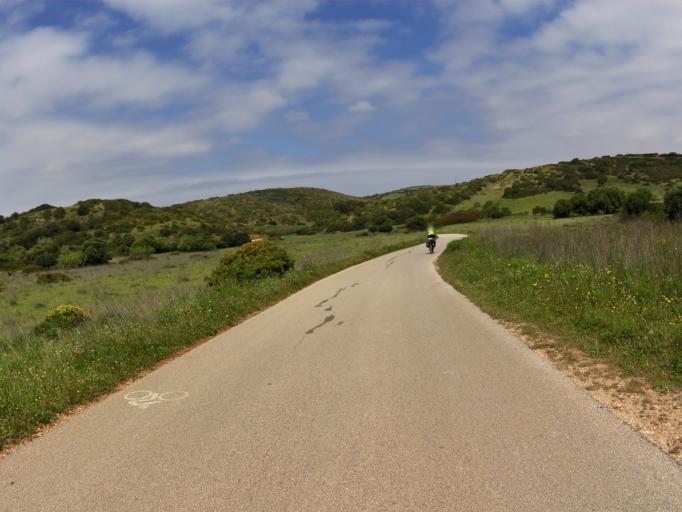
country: PT
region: Faro
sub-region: Vila do Bispo
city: Vila do Bispo
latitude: 37.0667
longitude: -8.8688
